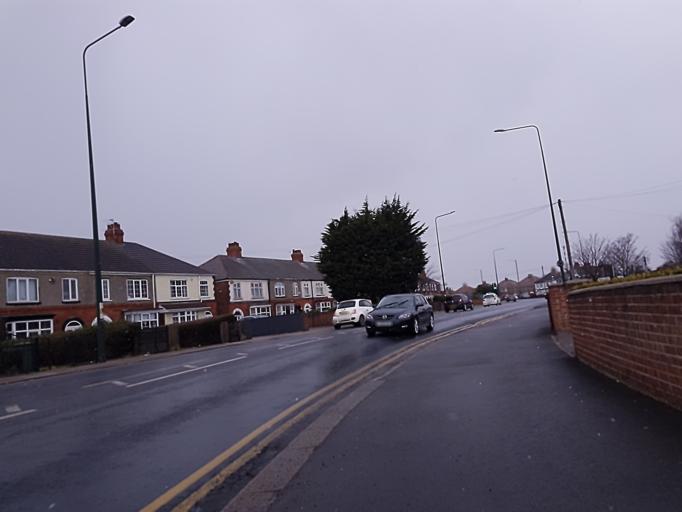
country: GB
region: England
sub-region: North East Lincolnshire
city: Grimbsy
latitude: 53.5621
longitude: -0.1141
